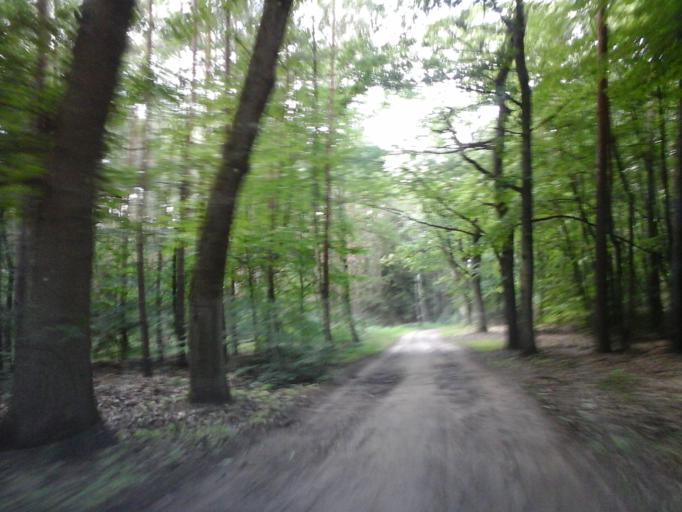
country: PL
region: West Pomeranian Voivodeship
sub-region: Powiat choszczenski
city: Bierzwnik
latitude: 53.0642
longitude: 15.6894
